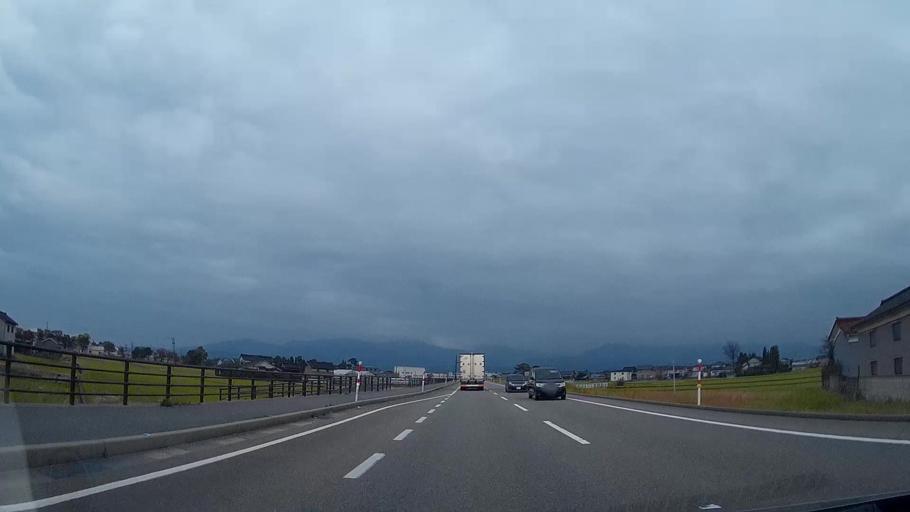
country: JP
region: Toyama
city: Nyuzen
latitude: 36.9277
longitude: 137.4828
